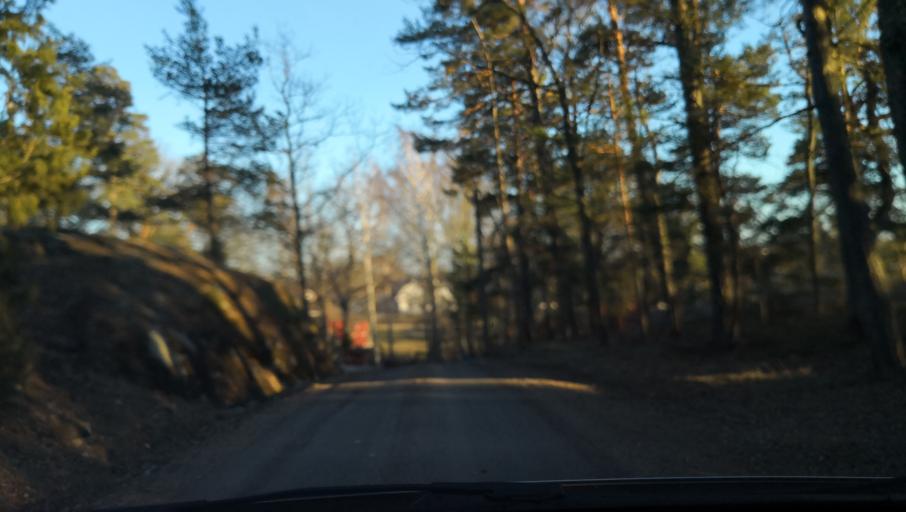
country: SE
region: Stockholm
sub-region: Varmdo Kommun
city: Mortnas
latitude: 59.3340
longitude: 18.4454
